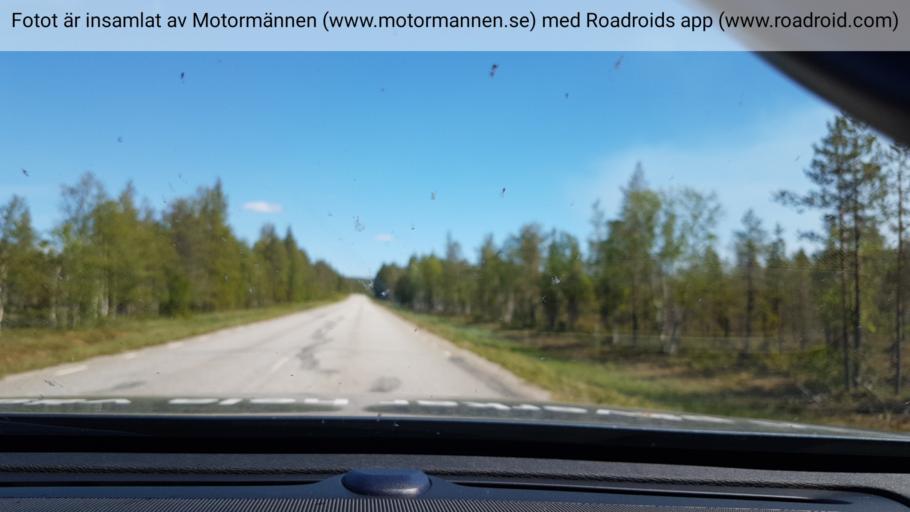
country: SE
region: Vaesterbotten
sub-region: Lycksele Kommun
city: Soderfors
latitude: 64.6922
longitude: 17.7664
